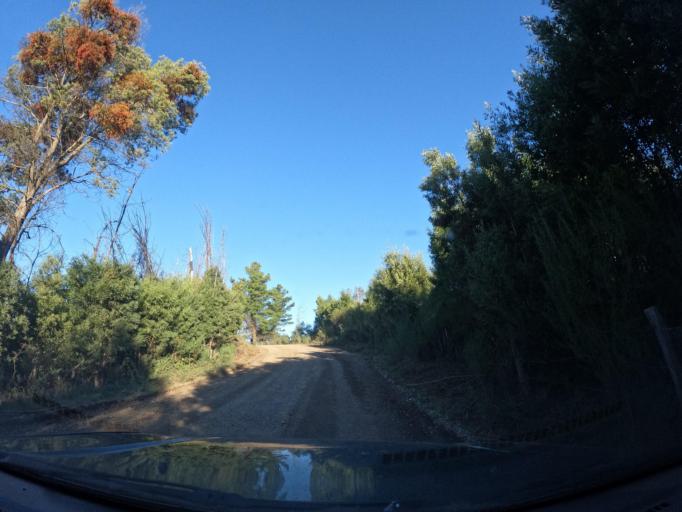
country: CL
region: Biobio
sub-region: Provincia de Concepcion
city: Chiguayante
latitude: -37.0326
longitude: -72.8686
